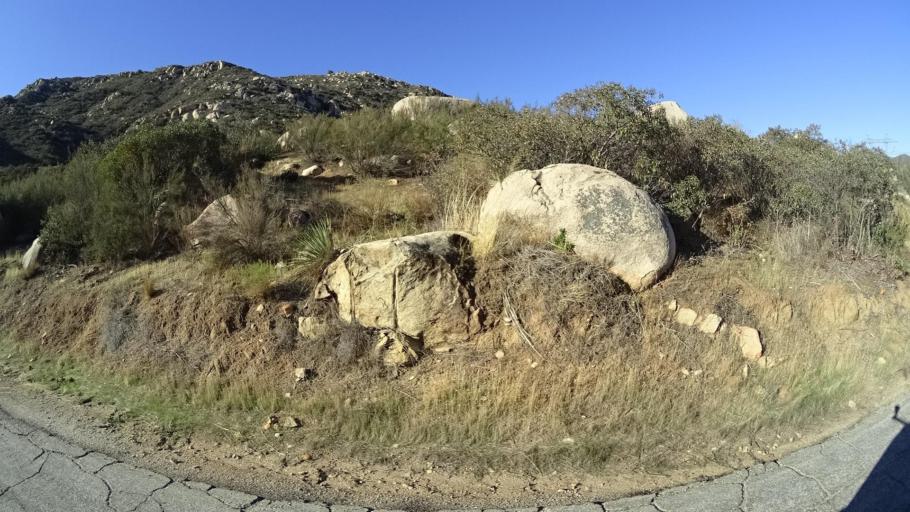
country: MX
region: Baja California
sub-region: Tecate
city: Lomas de Santa Anita
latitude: 32.6045
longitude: -116.6912
